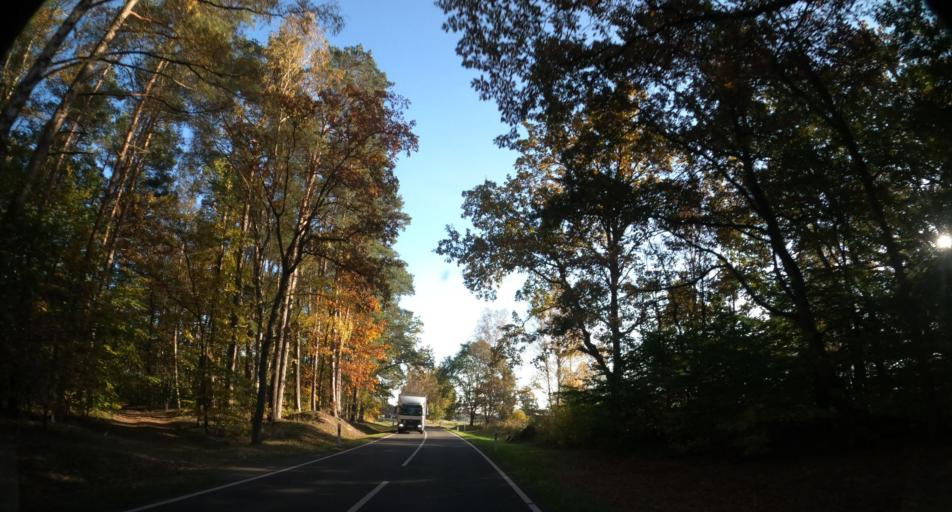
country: DE
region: Mecklenburg-Vorpommern
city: Ahlbeck
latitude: 53.6485
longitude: 14.1916
